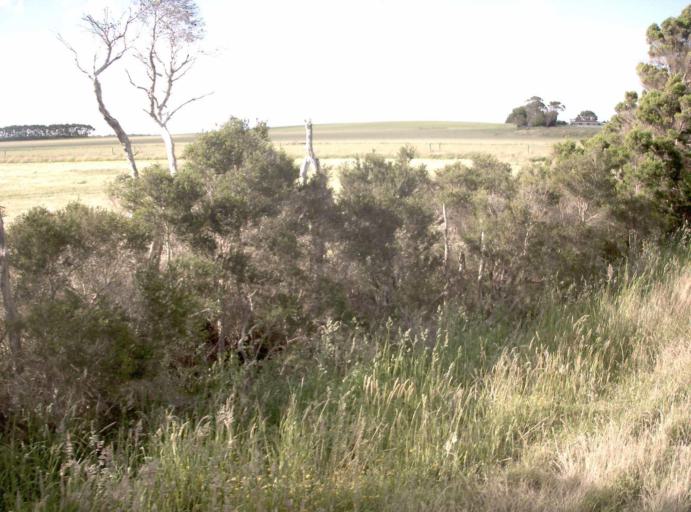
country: AU
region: Victoria
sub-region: Bass Coast
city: North Wonthaggi
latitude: -38.6199
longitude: 145.7374
